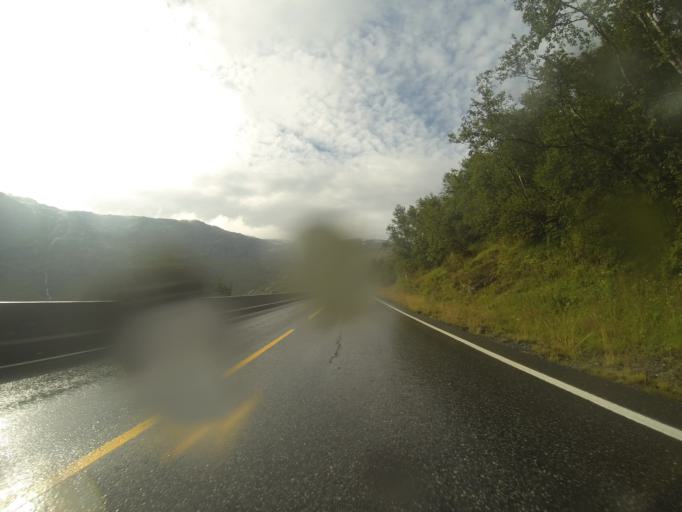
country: NO
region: Hordaland
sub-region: Odda
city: Odda
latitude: 59.8211
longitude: 6.7467
